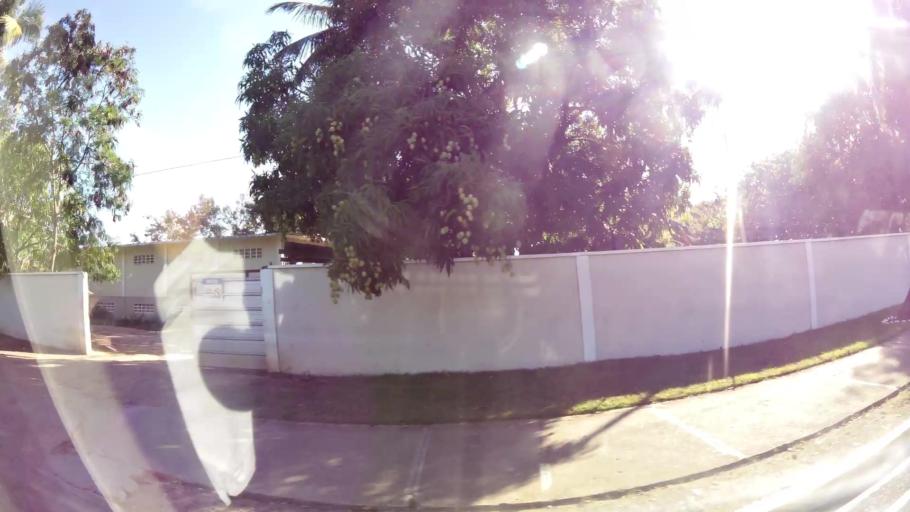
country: DO
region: Nacional
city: Ciudad Nueva
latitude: 18.4733
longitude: -69.8764
